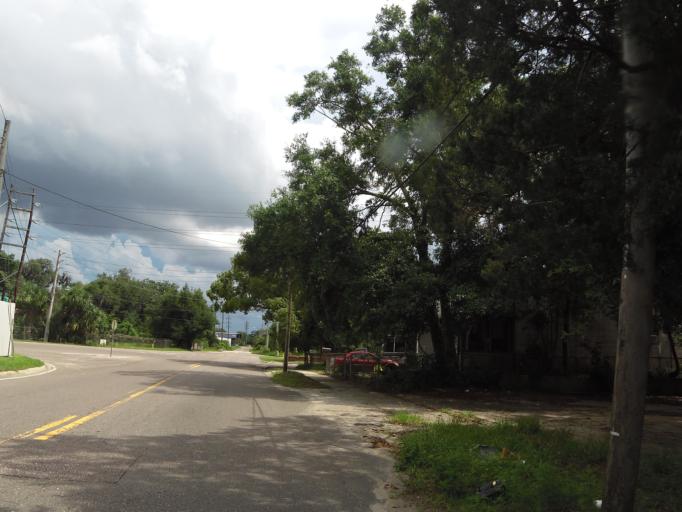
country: US
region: Florida
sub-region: Duval County
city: Jacksonville
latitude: 30.3732
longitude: -81.6400
